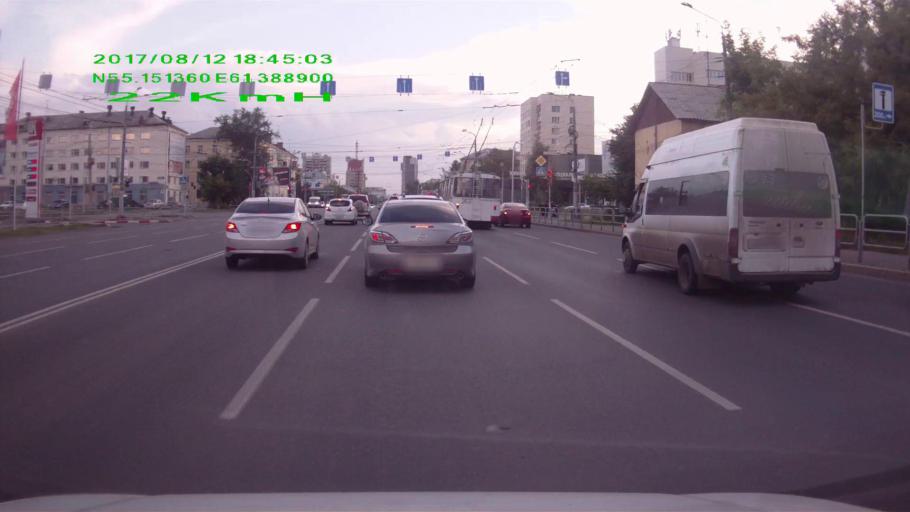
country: RU
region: Chelyabinsk
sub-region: Gorod Chelyabinsk
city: Chelyabinsk
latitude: 55.1486
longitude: 61.3849
